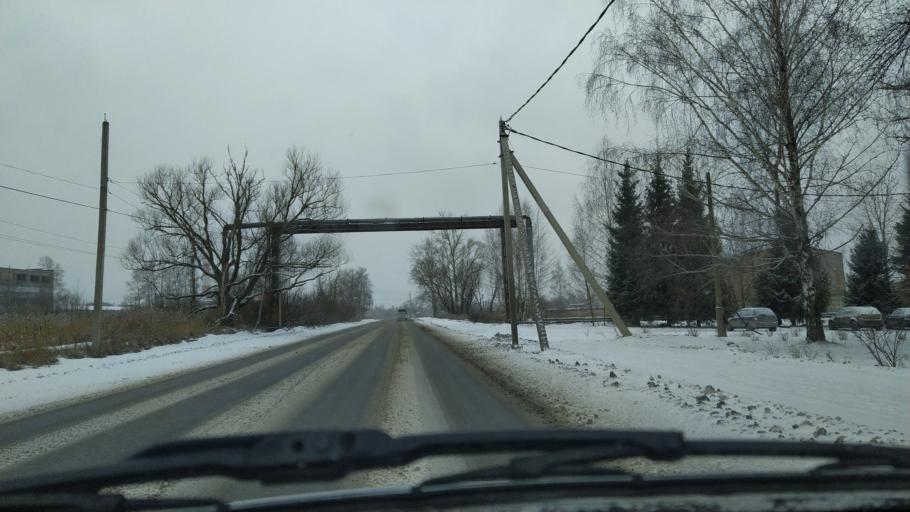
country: RU
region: Moskovskaya
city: Lopatinskiy
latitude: 55.3477
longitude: 38.7371
